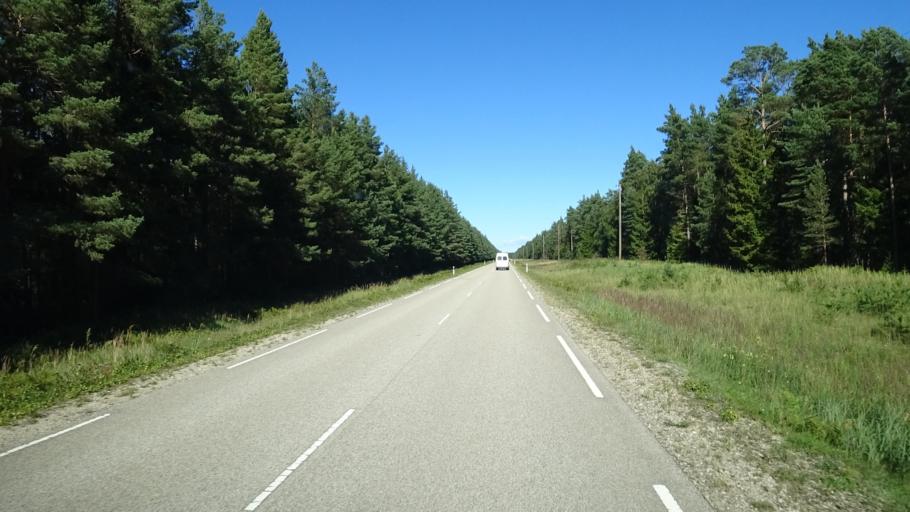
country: LV
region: Dundaga
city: Dundaga
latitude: 57.7276
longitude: 22.4995
